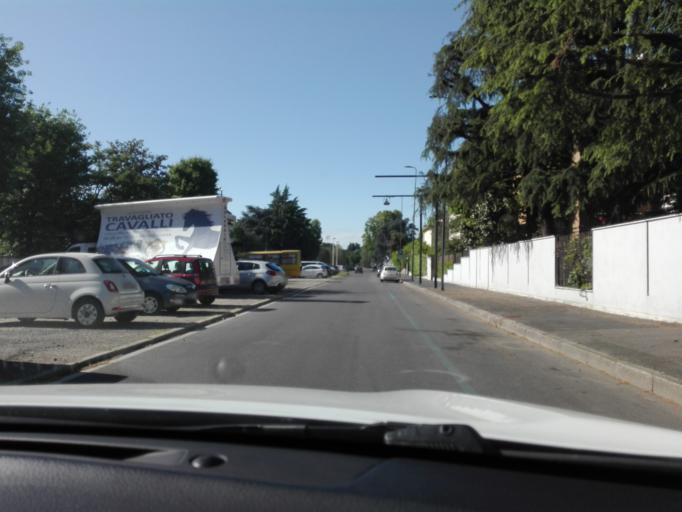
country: IT
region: Lombardy
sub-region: Citta metropolitana di Milano
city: Romano Banco
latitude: 45.4763
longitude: 9.1322
